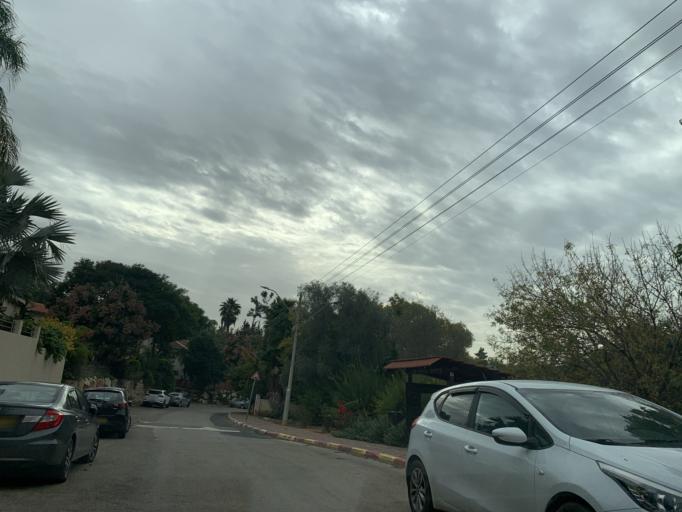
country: IL
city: Nirit
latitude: 32.1451
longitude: 34.9855
